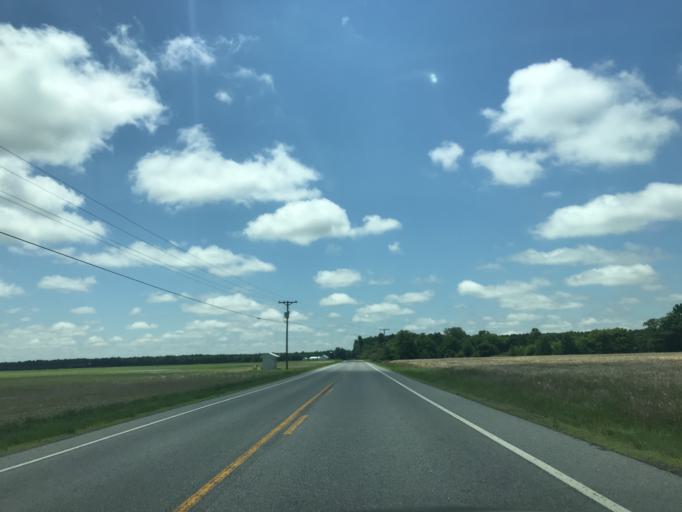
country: US
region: Maryland
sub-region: Caroline County
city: Federalsburg
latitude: 38.7300
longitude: -75.7311
